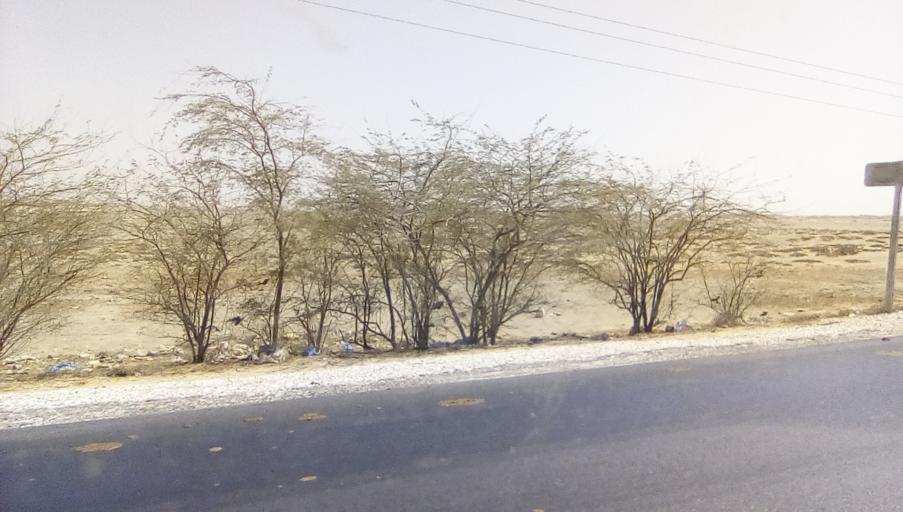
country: SN
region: Saint-Louis
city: Saint-Louis
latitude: 16.0396
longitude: -16.4499
